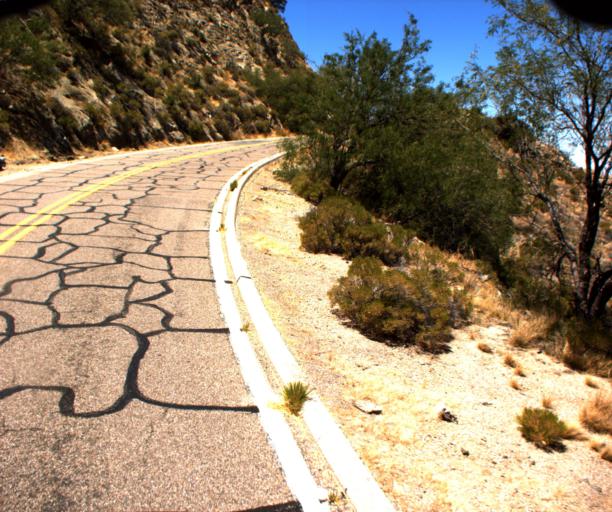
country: US
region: Arizona
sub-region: Pima County
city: Three Points
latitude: 31.9873
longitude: -111.5947
